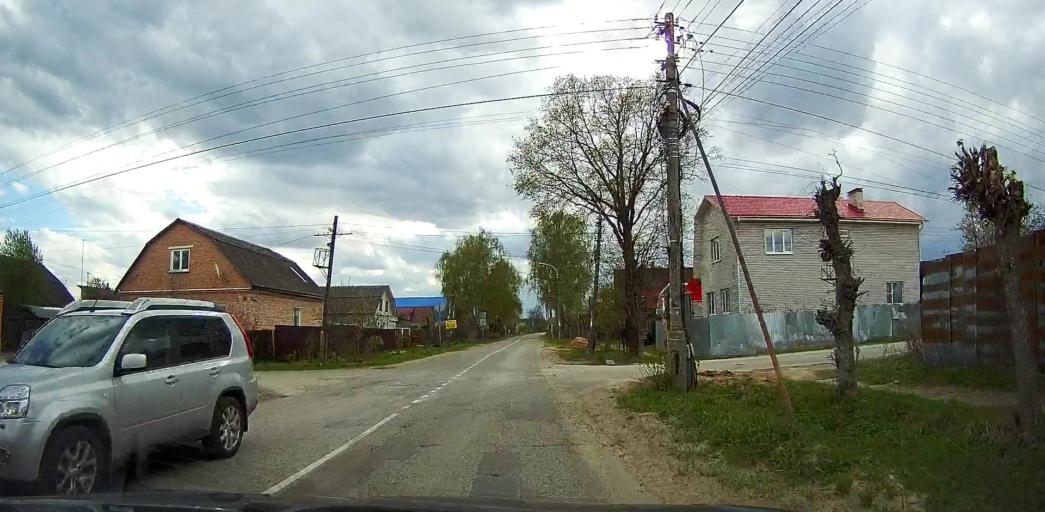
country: RU
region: Moskovskaya
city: Pavlovskiy Posad
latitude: 55.7765
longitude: 38.6342
